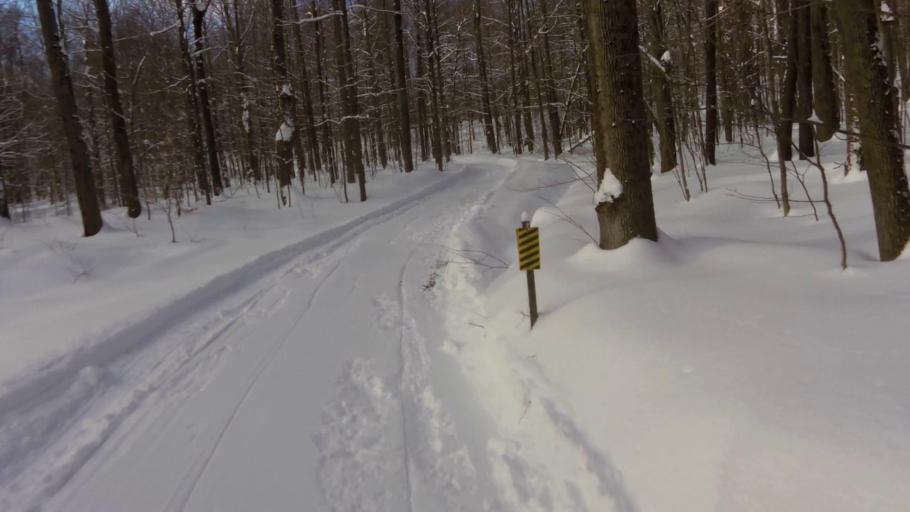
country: US
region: New York
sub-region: Chautauqua County
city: Falconer
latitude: 42.2463
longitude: -79.1510
